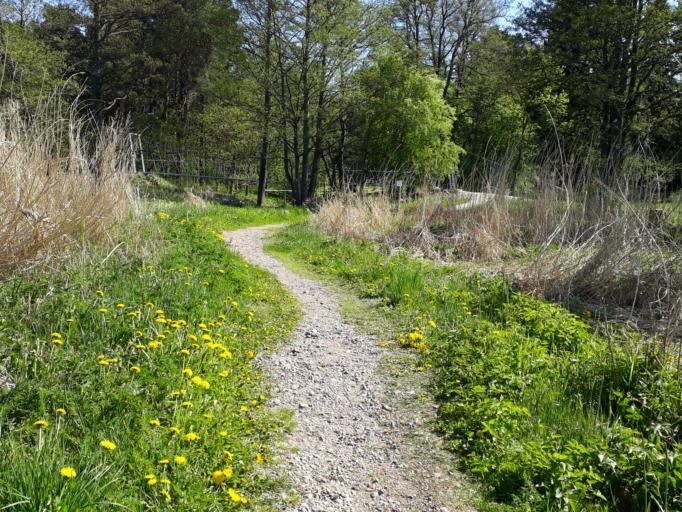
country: EE
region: Laeaene-Virumaa
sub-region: Haljala vald
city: Haljala
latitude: 59.5863
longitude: 26.1177
